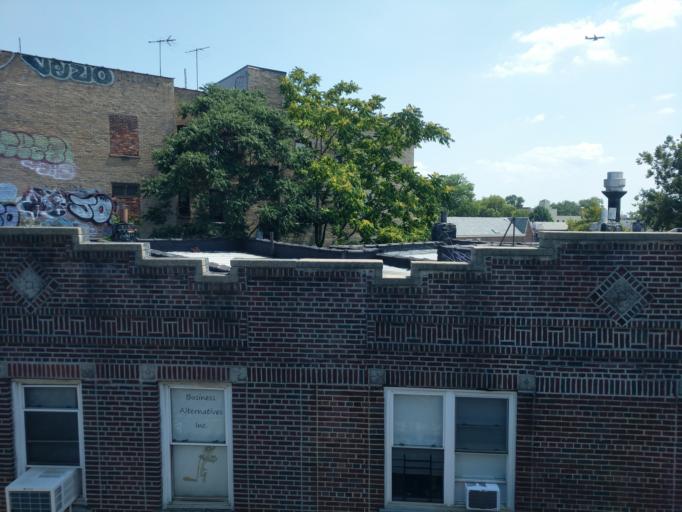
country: US
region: New York
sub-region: Bronx
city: Eastchester
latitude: 40.8515
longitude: -73.8296
